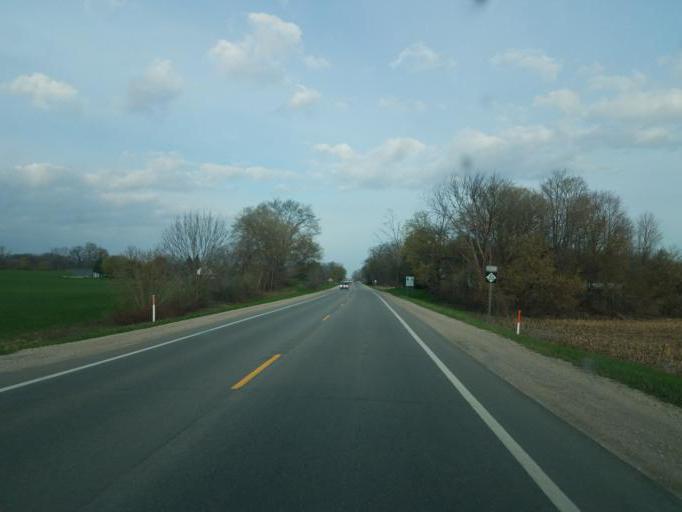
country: US
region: Michigan
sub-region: Isabella County
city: Mount Pleasant
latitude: 43.5978
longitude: -84.8677
